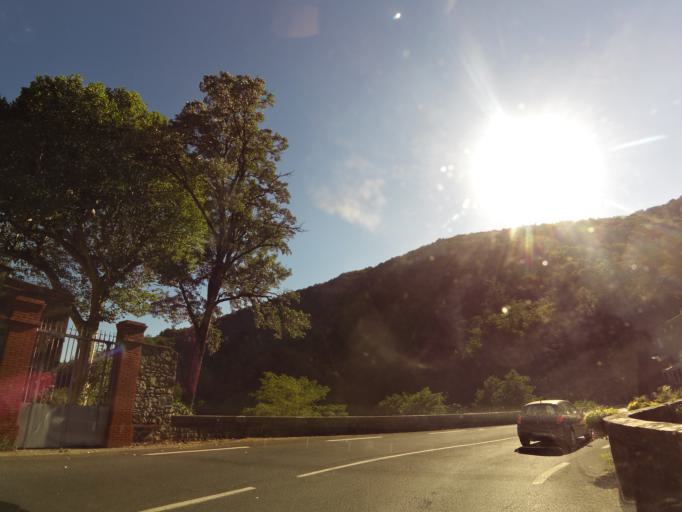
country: FR
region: Languedoc-Roussillon
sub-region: Departement du Gard
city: Valleraugue
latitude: 44.0592
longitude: 3.6855
